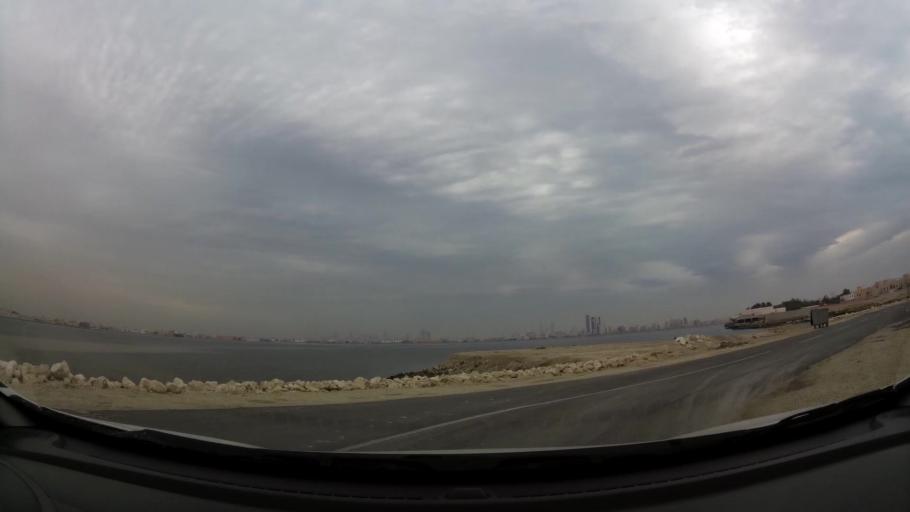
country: BH
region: Northern
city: Madinat `Isa
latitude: 26.1816
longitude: 50.5795
